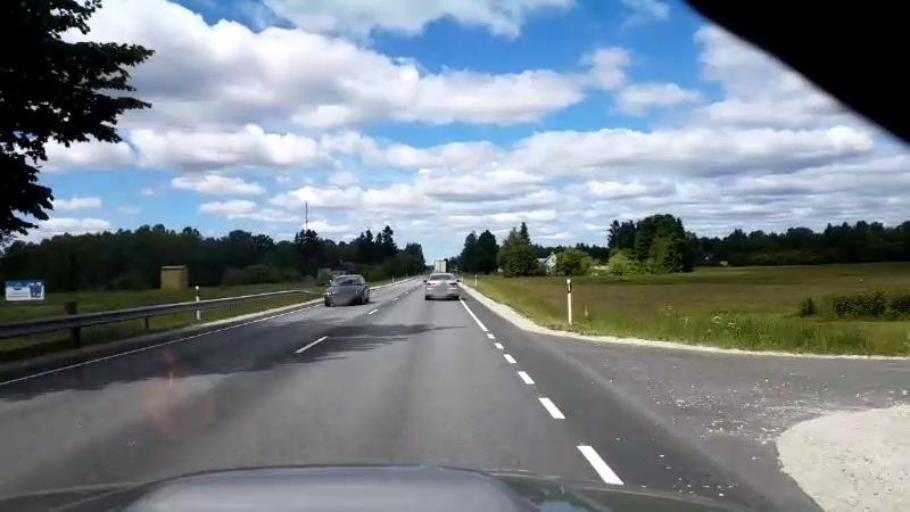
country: EE
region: Paernumaa
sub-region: Halinga vald
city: Parnu-Jaagupi
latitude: 58.6547
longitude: 24.4756
